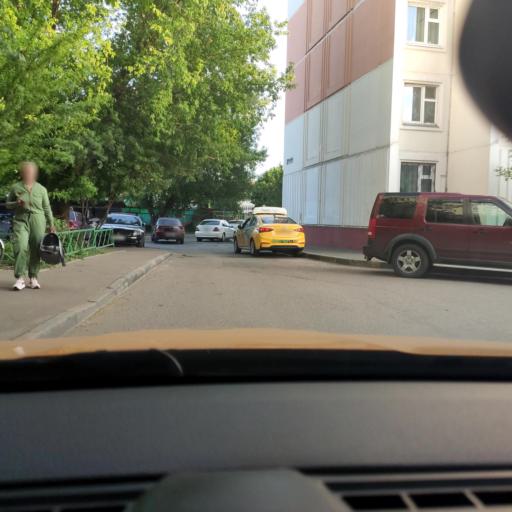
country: RU
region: Moscow
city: Nekrasovka
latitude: 55.6944
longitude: 37.8989
